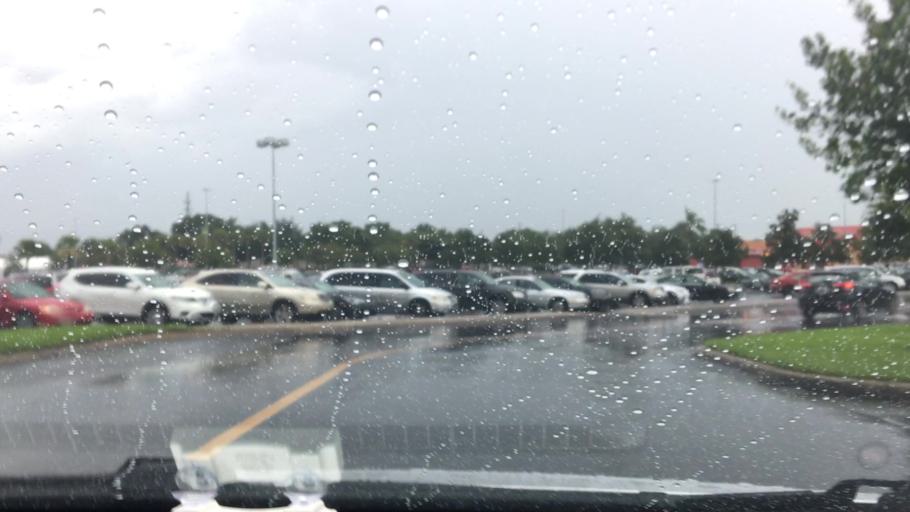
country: US
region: Florida
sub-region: Seminole County
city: Altamonte Springs
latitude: 28.6651
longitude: -81.3766
